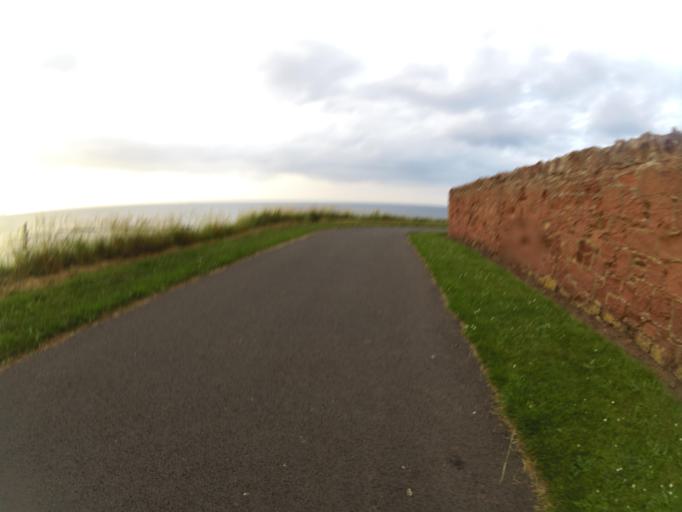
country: GB
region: Scotland
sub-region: East Lothian
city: Dunbar
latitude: 56.0060
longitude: -2.5326
